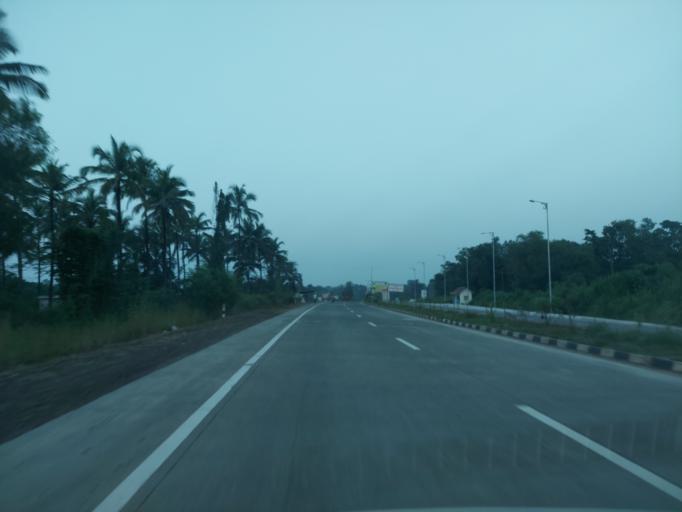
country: IN
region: Maharashtra
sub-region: Sindhudurg
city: Kudal
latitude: 16.1023
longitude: 73.7084
